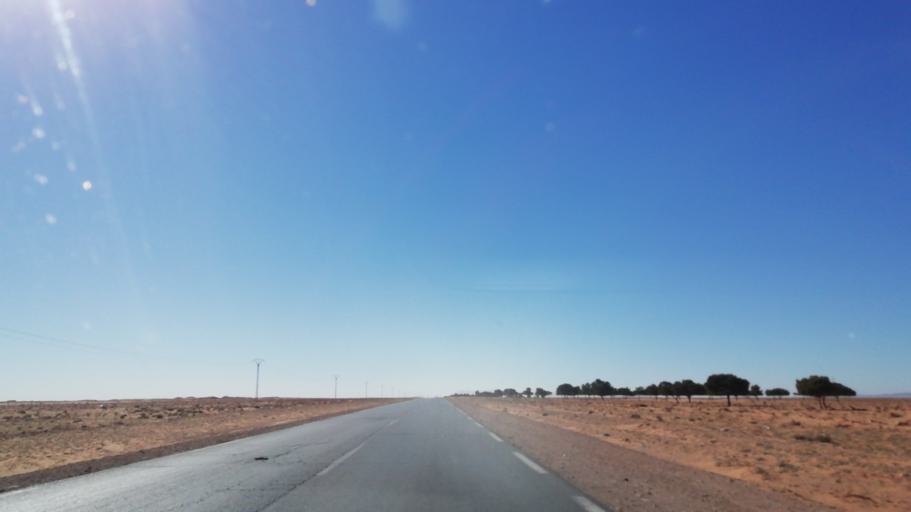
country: DZ
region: Saida
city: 'Ain el Hadjar
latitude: 33.9823
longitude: 0.0294
